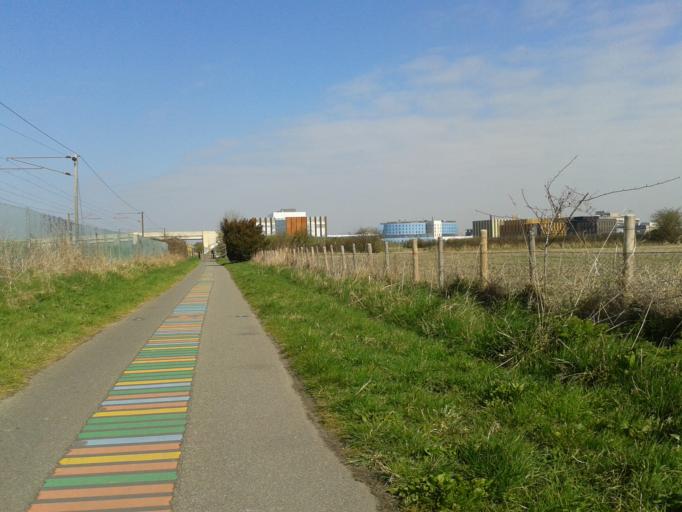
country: GB
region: England
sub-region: Cambridgeshire
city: Cambridge
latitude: 52.1657
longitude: 0.1325
